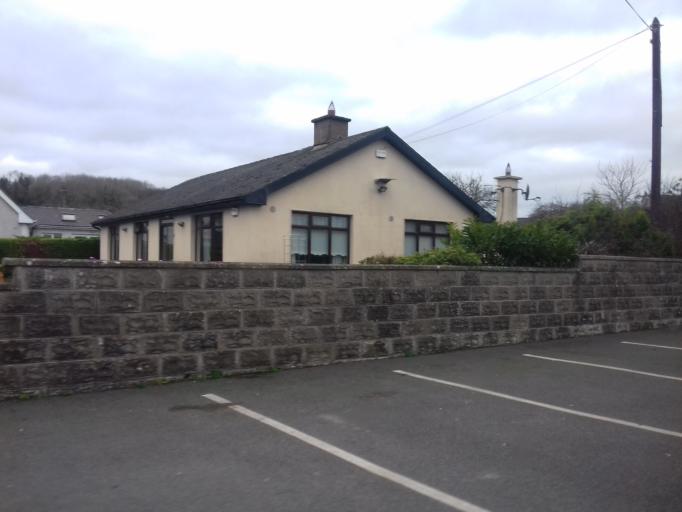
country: IE
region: Leinster
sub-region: An Mhi
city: Duleek
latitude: 53.6920
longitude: -6.4159
